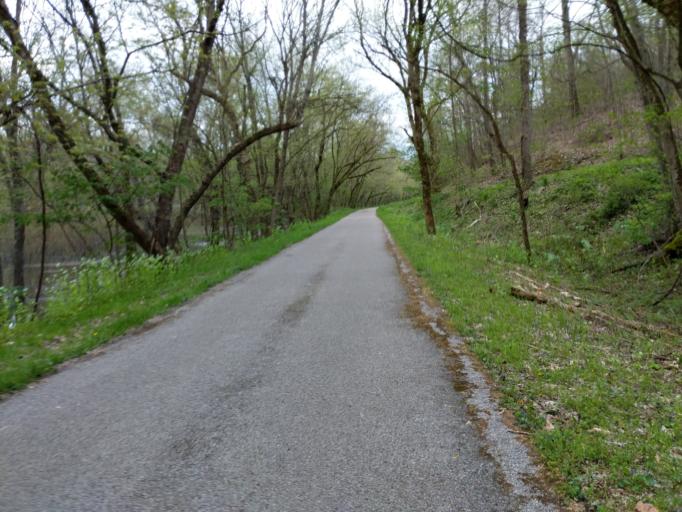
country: US
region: Ohio
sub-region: Athens County
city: Chauncey
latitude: 39.3866
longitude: -82.1214
